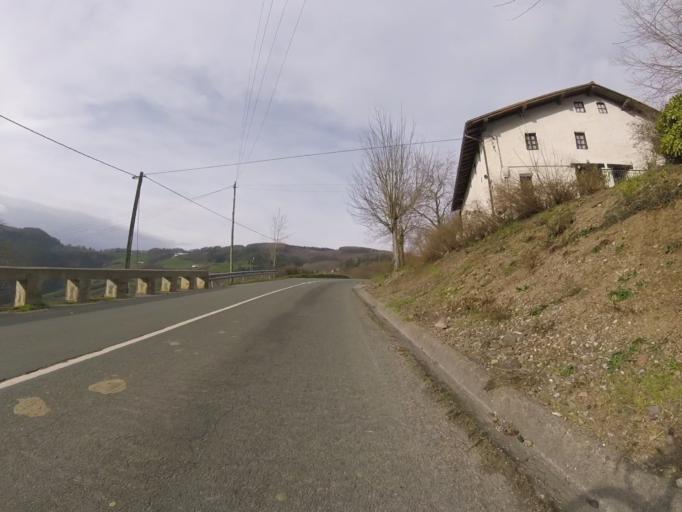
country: ES
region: Basque Country
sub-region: Provincia de Guipuzcoa
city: Errezil
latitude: 43.1440
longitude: -2.1752
